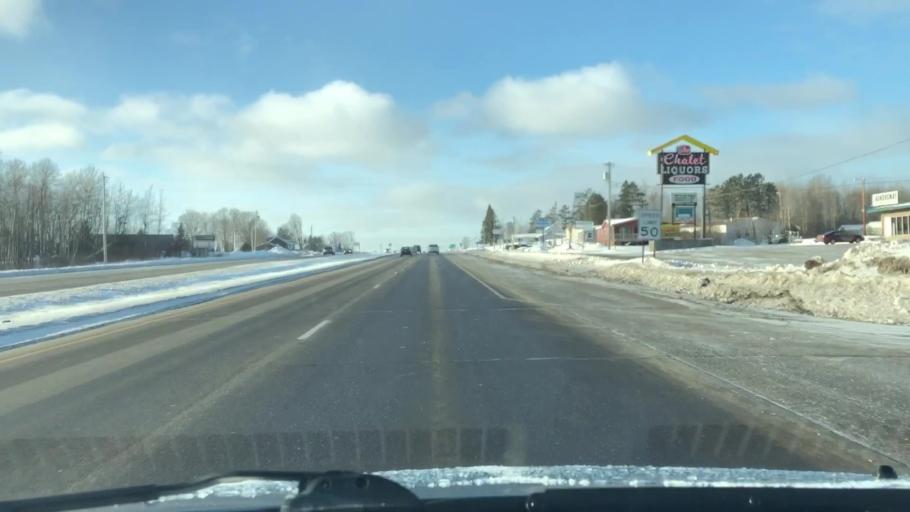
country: US
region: Minnesota
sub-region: Saint Louis County
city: Hermantown
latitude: 46.8234
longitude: -92.1887
